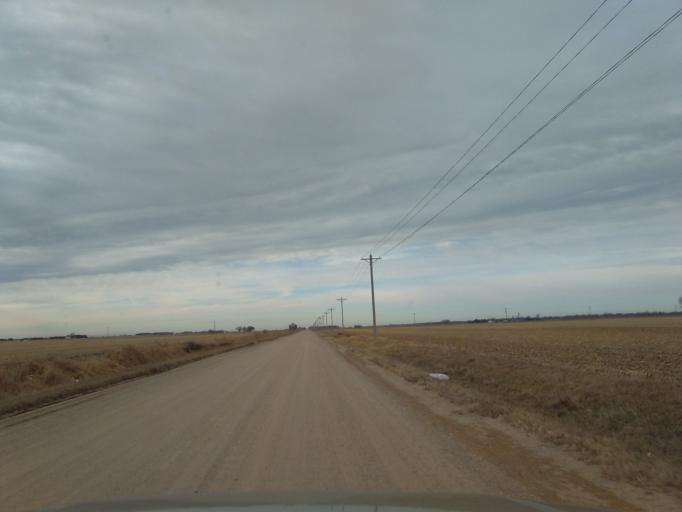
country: US
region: Nebraska
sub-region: Buffalo County
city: Gibbon
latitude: 40.6408
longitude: -98.9079
